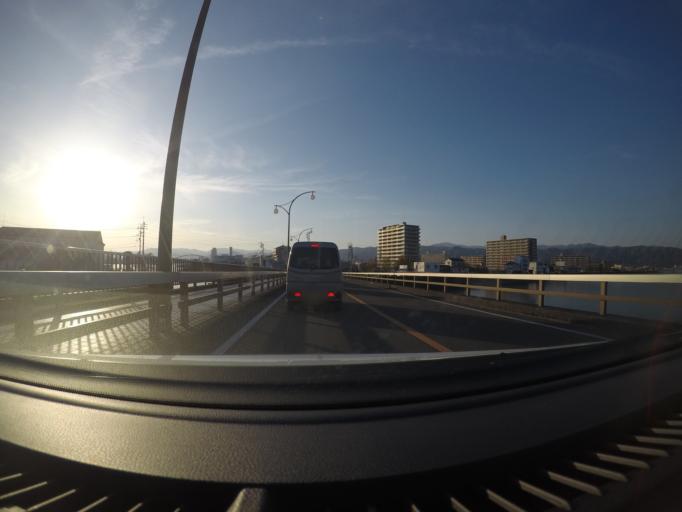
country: JP
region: Kochi
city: Kochi-shi
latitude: 33.5508
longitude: 133.5657
